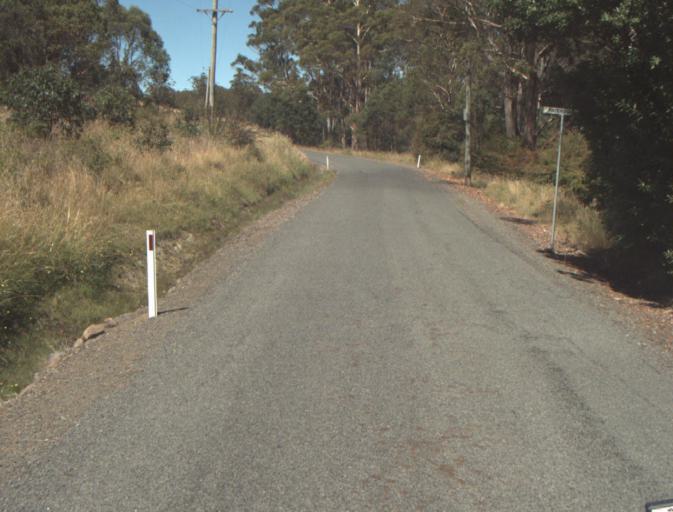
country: AU
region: Tasmania
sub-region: Launceston
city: Newstead
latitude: -41.3559
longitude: 147.3030
